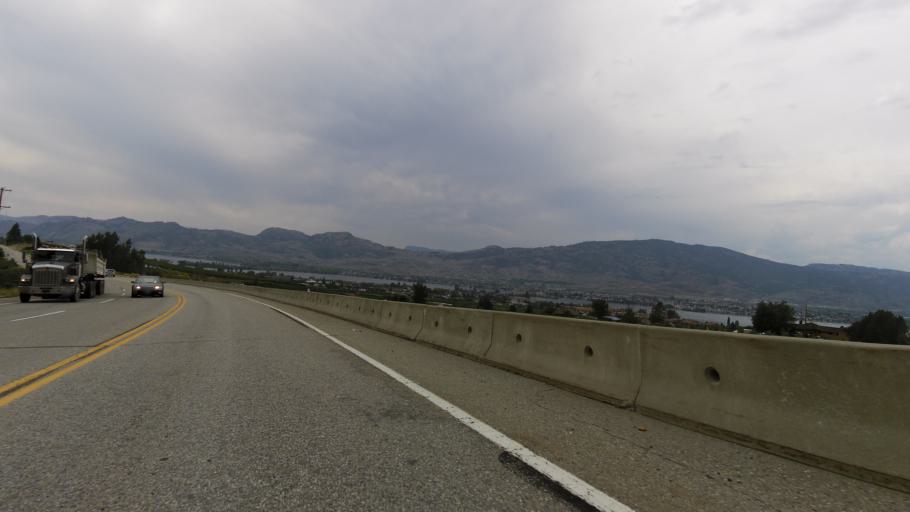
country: CA
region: British Columbia
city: Osoyoos
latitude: 49.0369
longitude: -119.4297
